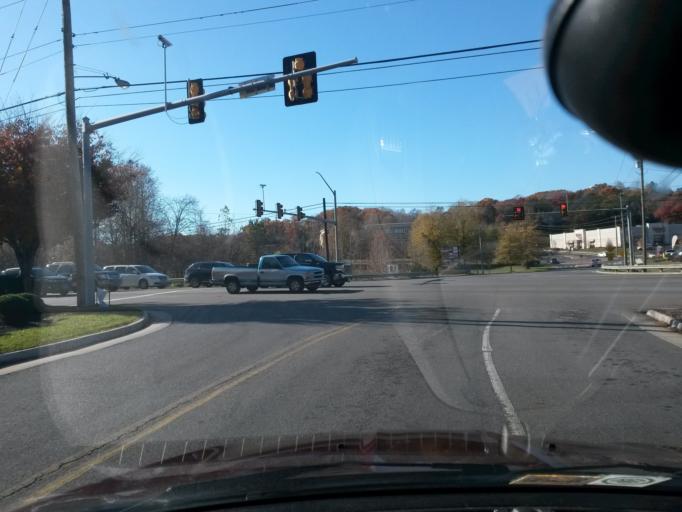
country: US
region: Virginia
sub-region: City of Lynchburg
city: West Lynchburg
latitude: 37.3489
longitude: -79.1855
